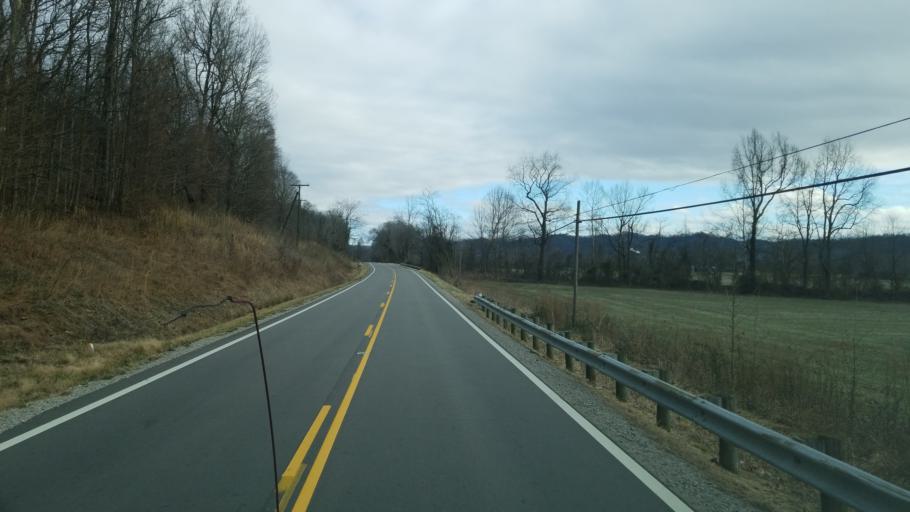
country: US
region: Kentucky
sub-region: Lewis County
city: Vanceburg
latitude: 38.6268
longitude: -83.2008
